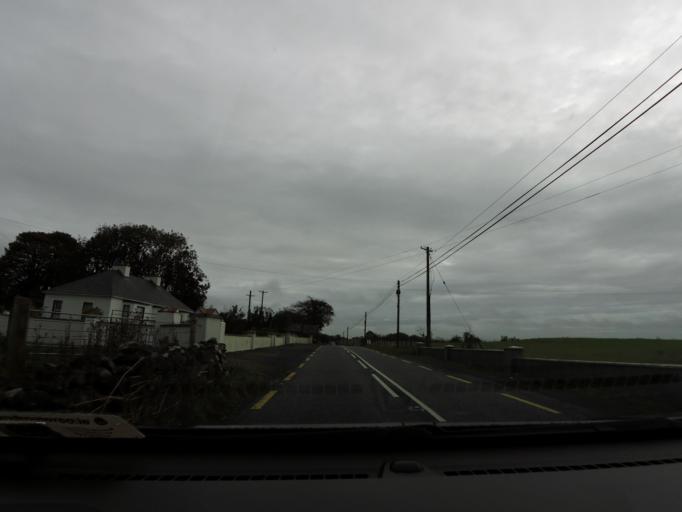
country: IE
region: Connaught
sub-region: County Galway
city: Tuam
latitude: 53.5953
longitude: -8.7692
